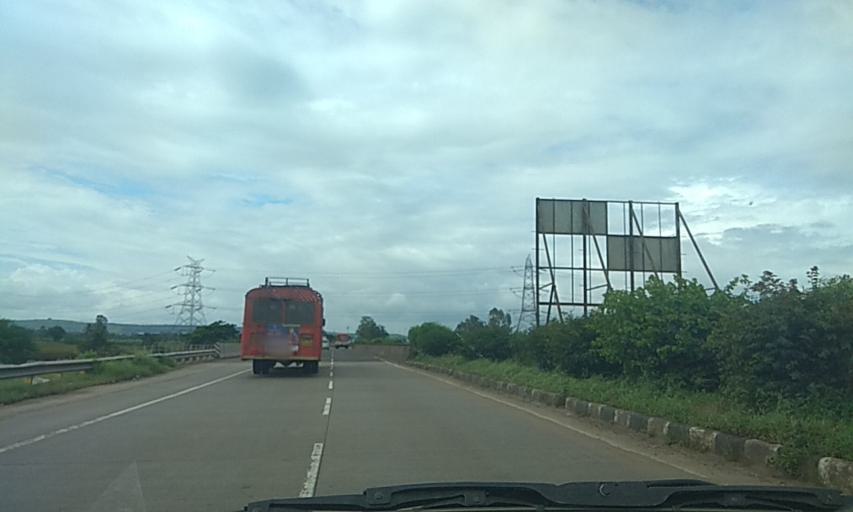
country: IN
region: Maharashtra
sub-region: Kolhapur
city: Kagal
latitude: 16.5533
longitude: 74.3181
